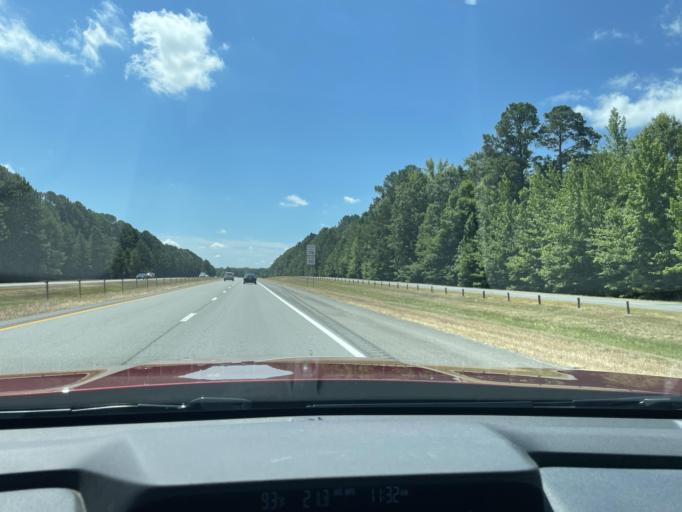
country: US
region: Arkansas
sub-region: Jefferson County
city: Redfield
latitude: 34.5009
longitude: -92.2145
